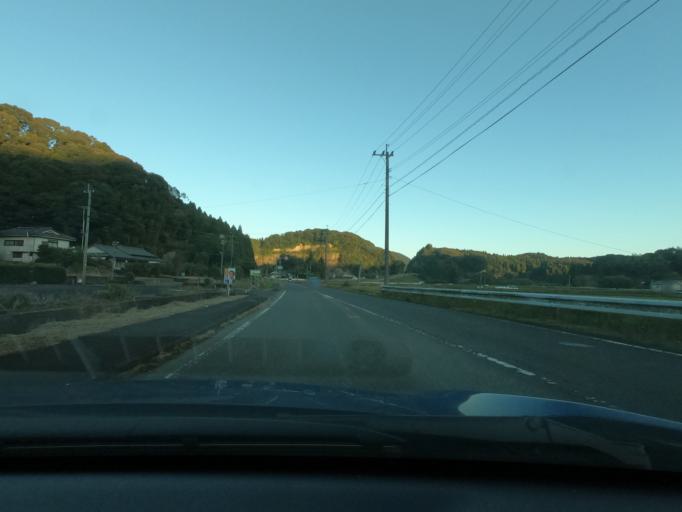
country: JP
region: Kagoshima
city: Satsumasendai
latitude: 31.8075
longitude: 130.3868
